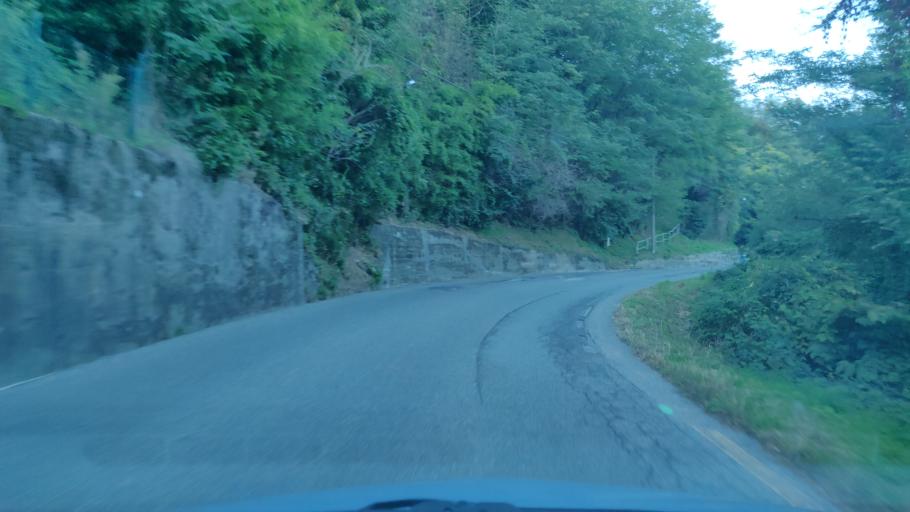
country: IT
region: Piedmont
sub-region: Provincia di Biella
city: Ronco Biellese
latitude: 45.5764
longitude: 8.0804
